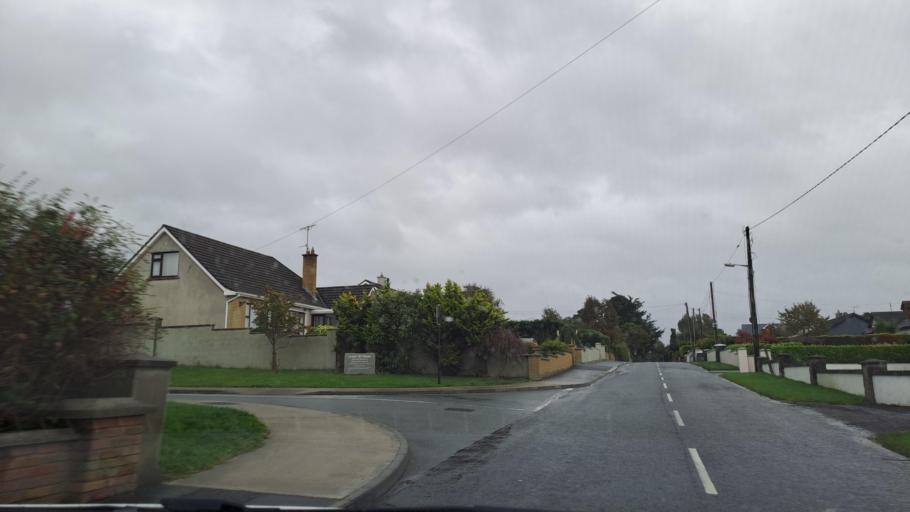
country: IE
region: Leinster
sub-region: Lu
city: Blackrock
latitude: 53.9632
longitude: -6.3852
